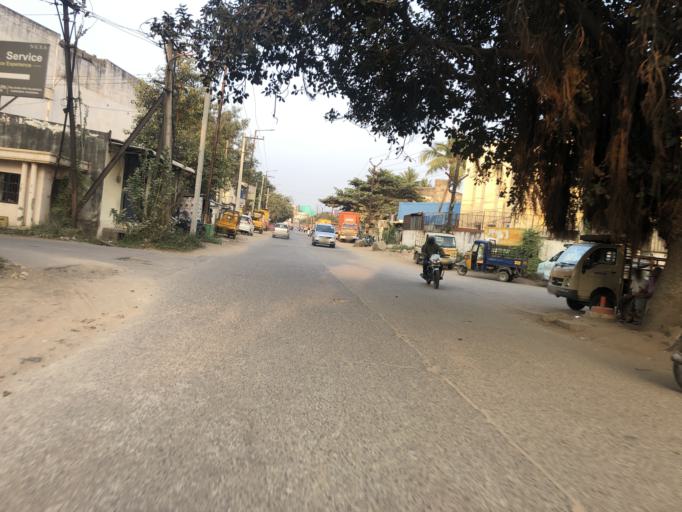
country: IN
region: Telangana
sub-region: Rangareddi
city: Kukatpalli
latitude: 17.4644
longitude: 78.4430
